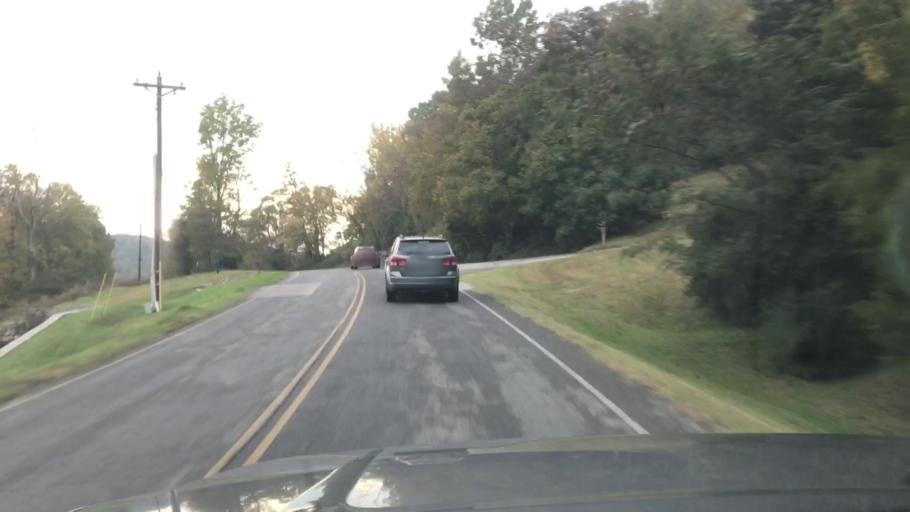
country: US
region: Tennessee
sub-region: Williamson County
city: Brentwood Estates
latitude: 36.0017
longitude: -86.8320
